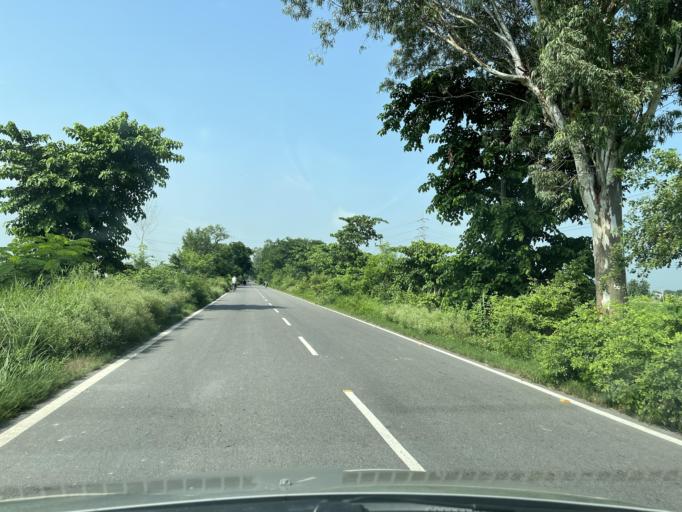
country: IN
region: Uttarakhand
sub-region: Udham Singh Nagar
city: Bazpur
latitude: 29.1955
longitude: 79.1970
